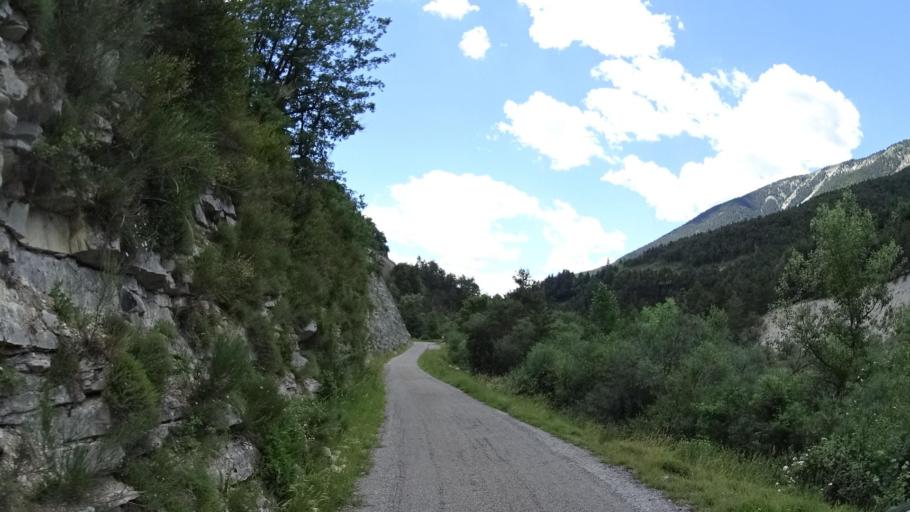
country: FR
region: Provence-Alpes-Cote d'Azur
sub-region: Departement des Alpes-de-Haute-Provence
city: Annot
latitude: 44.0219
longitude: 6.6294
